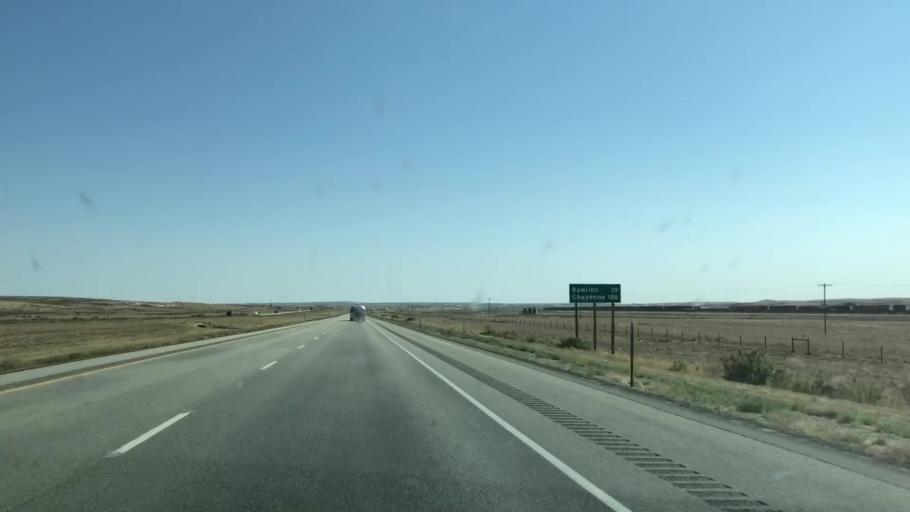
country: US
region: Wyoming
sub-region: Carbon County
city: Rawlins
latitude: 41.6835
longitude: -107.9604
